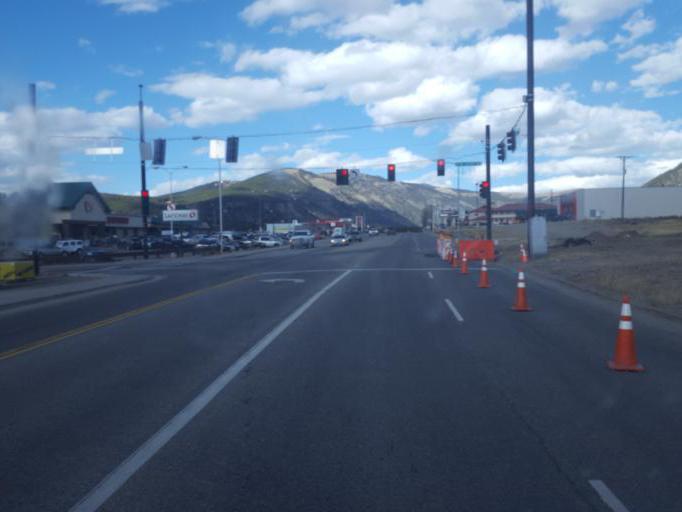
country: US
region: Colorado
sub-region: Lake County
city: Leadville
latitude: 39.2586
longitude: -106.2927
